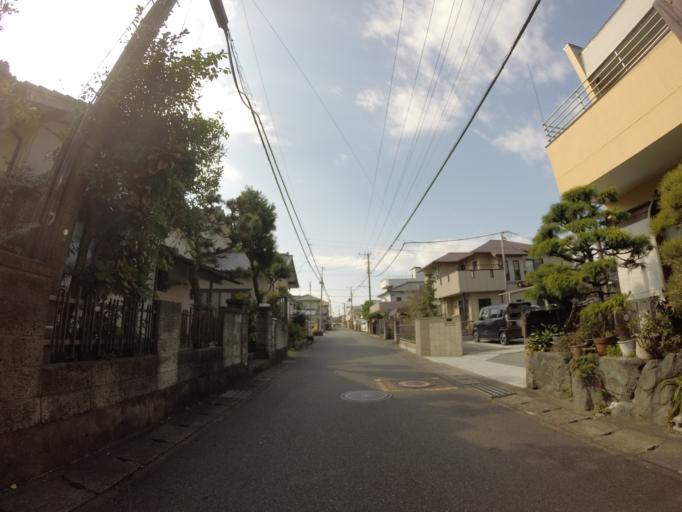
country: JP
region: Shizuoka
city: Fuji
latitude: 35.1317
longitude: 138.6750
